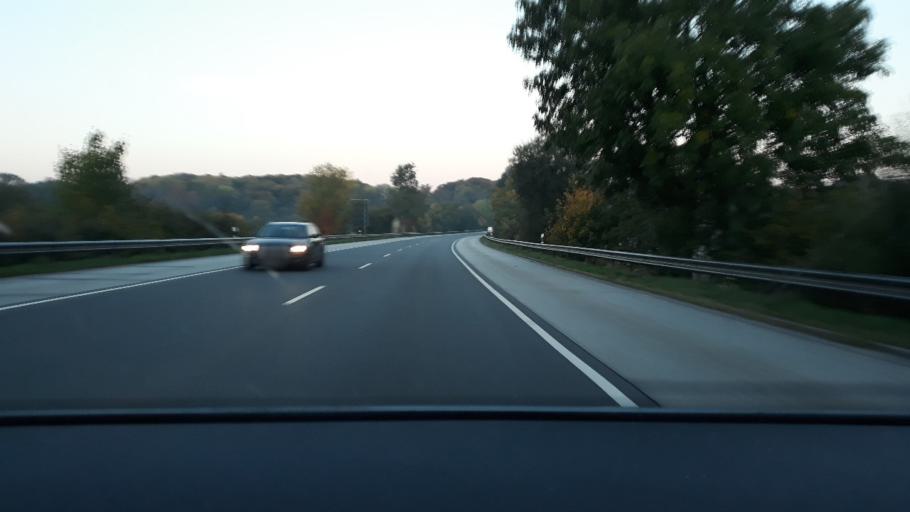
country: DE
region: Schleswig-Holstein
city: Busdorf
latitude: 54.5076
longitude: 9.5324
